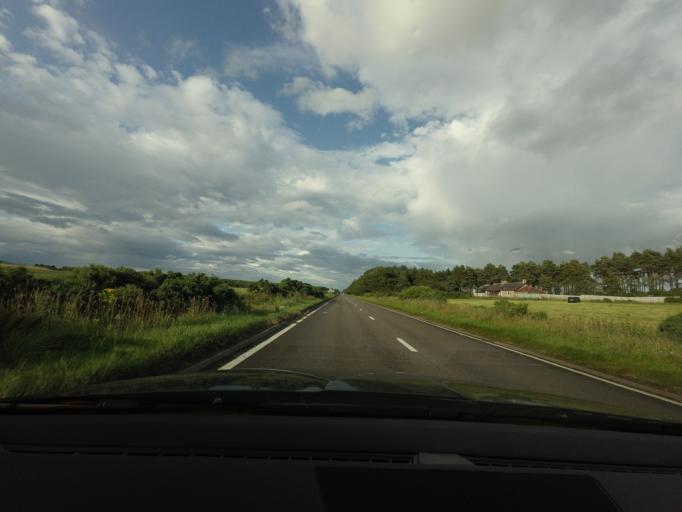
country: GB
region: Scotland
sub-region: Highland
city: Nairn
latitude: 57.5627
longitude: -3.9560
